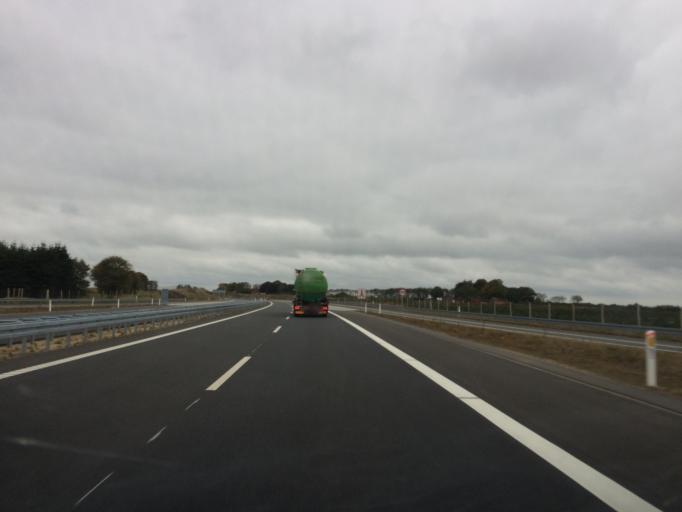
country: DK
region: Central Jutland
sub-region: Silkeborg Kommune
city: Silkeborg
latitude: 56.2020
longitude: 9.5485
